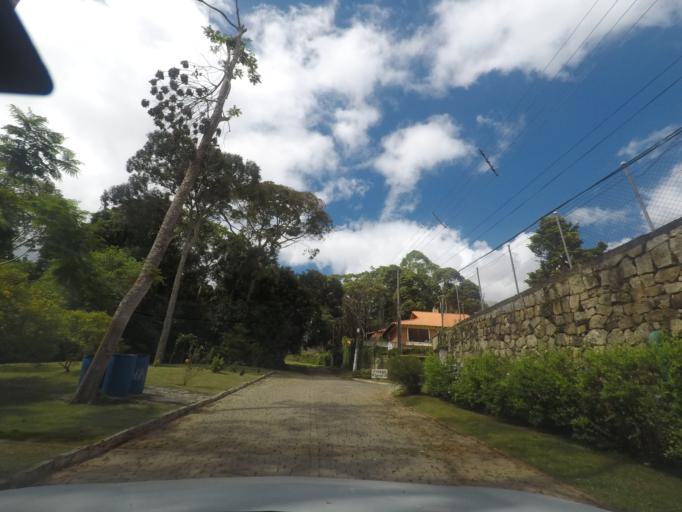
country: BR
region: Rio de Janeiro
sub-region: Teresopolis
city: Teresopolis
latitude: -22.3969
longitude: -42.9890
